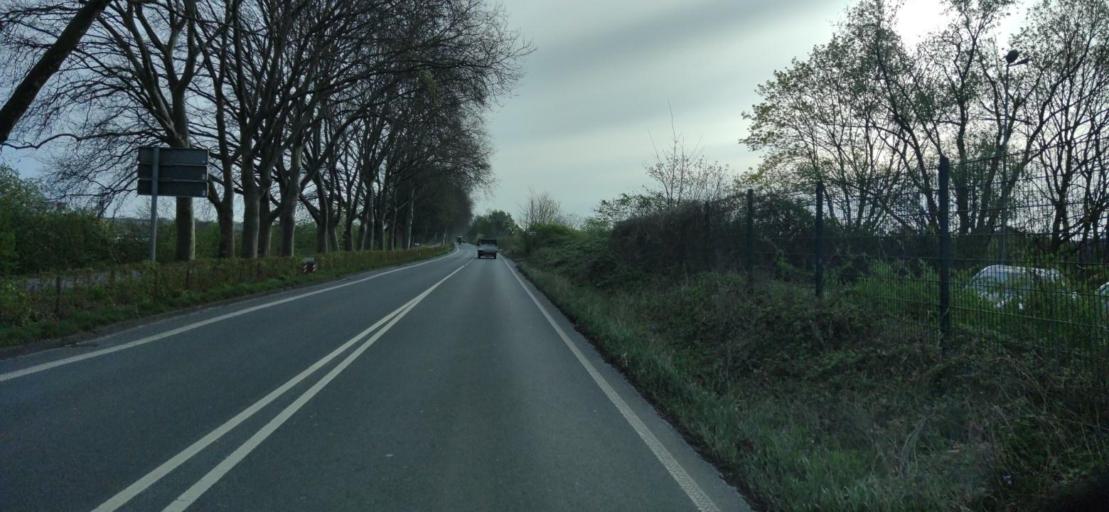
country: DE
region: North Rhine-Westphalia
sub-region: Regierungsbezirk Dusseldorf
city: Duisburg
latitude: 51.4441
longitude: 6.7644
